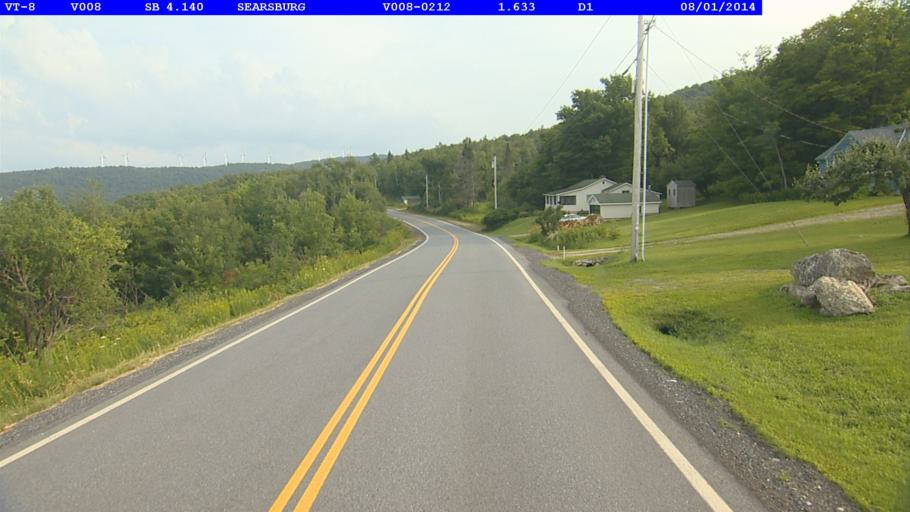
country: US
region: Vermont
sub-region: Windham County
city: Dover
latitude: 42.8805
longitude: -72.9712
